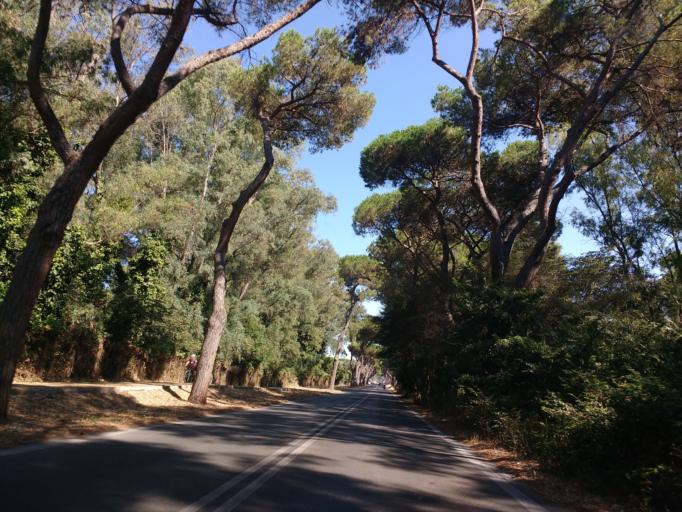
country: IT
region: Latium
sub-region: Citta metropolitana di Roma Capitale
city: Acilia-Castel Fusano-Ostia Antica
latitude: 41.7498
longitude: 12.3100
